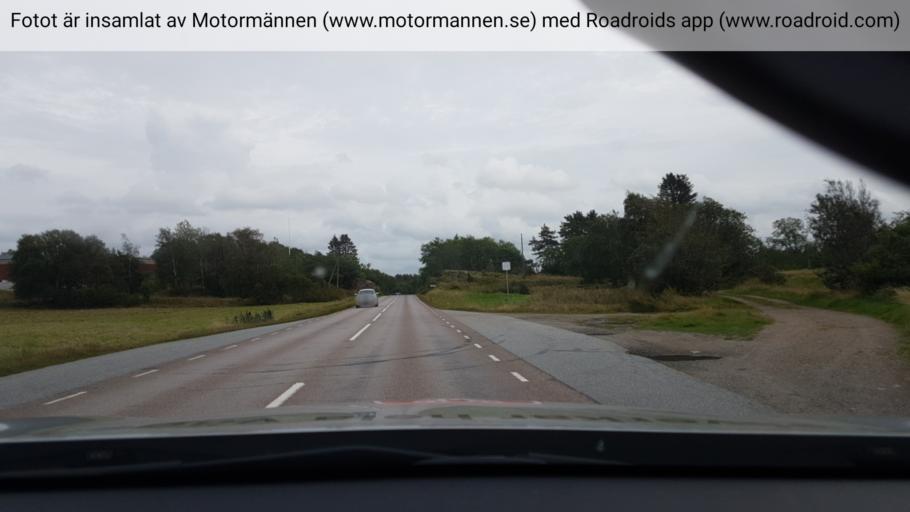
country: SE
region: Vaestra Goetaland
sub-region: Tanums Kommun
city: Grebbestad
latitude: 58.5955
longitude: 11.3077
